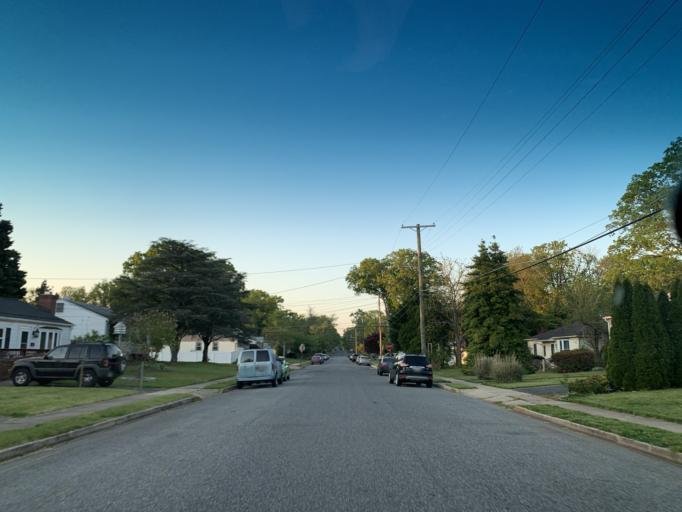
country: US
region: Maryland
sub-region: Harford County
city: Aberdeen
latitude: 39.5025
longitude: -76.1735
